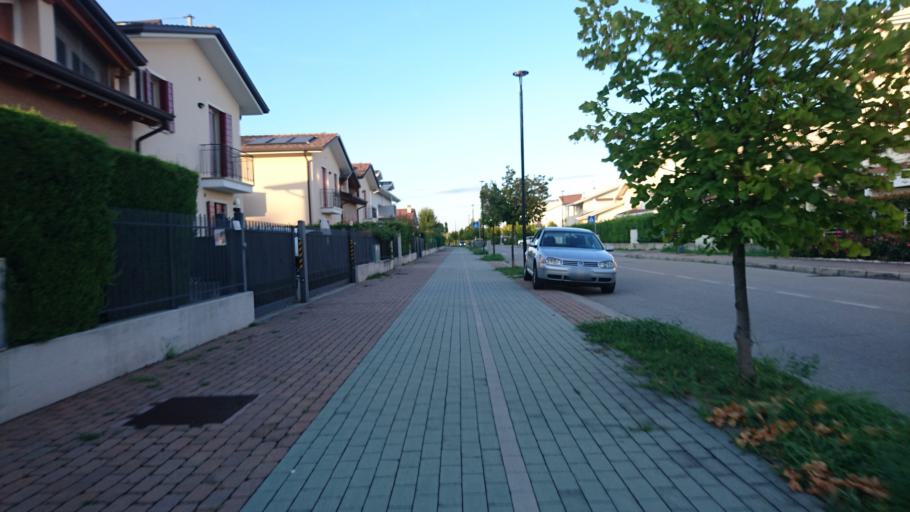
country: IT
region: Veneto
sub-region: Provincia di Padova
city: Montegrotto Terme
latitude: 45.3441
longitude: 11.7921
